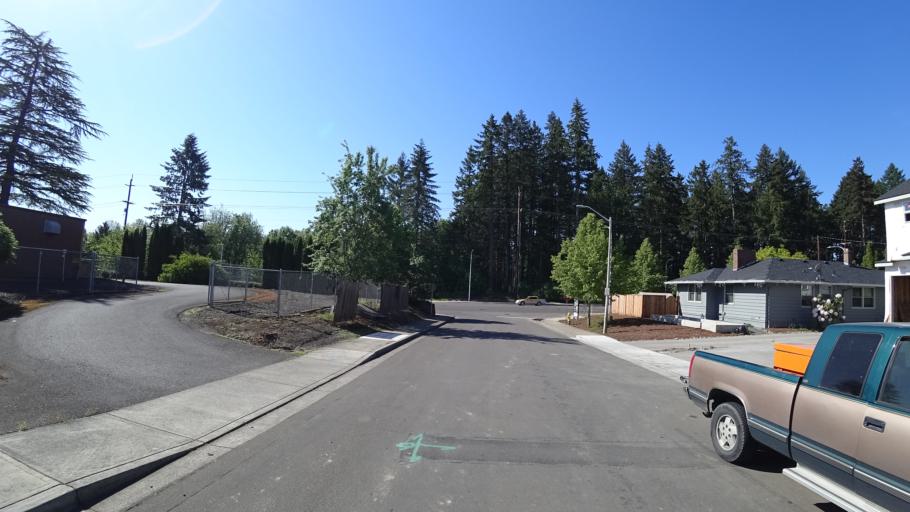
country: US
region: Oregon
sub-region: Washington County
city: Rockcreek
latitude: 45.5205
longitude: -122.9174
